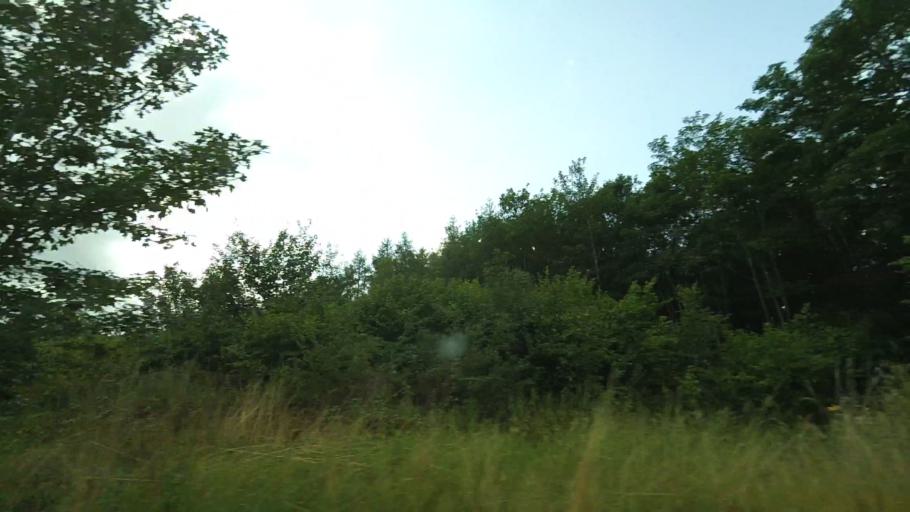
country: DK
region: Central Jutland
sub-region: Norddjurs Kommune
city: Allingabro
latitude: 56.4979
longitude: 10.3499
